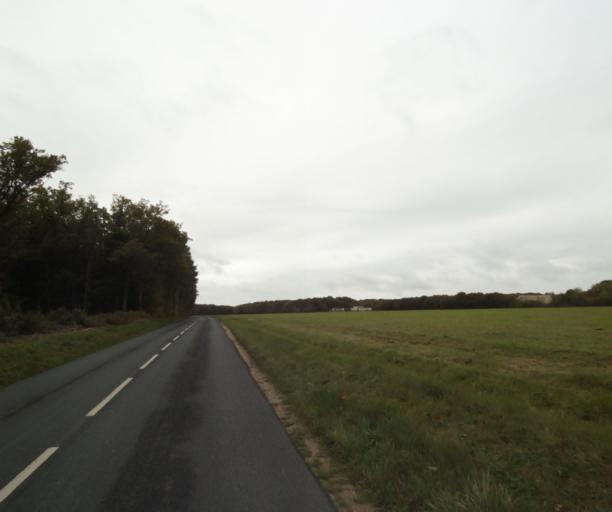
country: FR
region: Centre
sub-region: Departement d'Eure-et-Loir
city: Dreux
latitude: 48.7647
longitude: 1.3691
